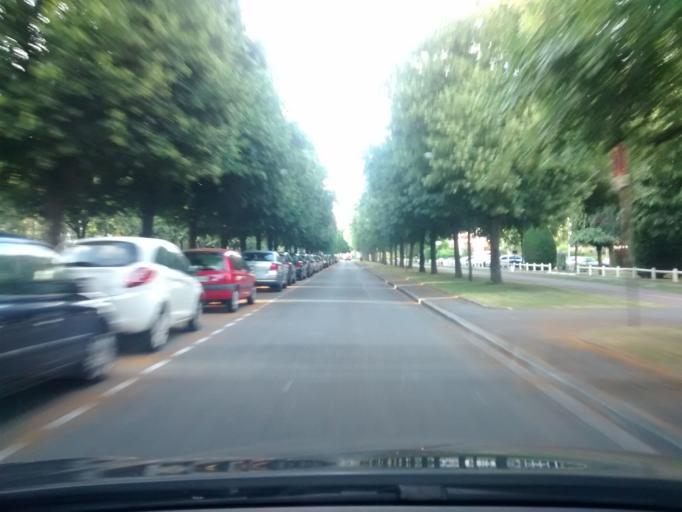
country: FR
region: Ile-de-France
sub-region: Departement des Yvelines
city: Le Chesnay
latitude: 48.8246
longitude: 2.1185
